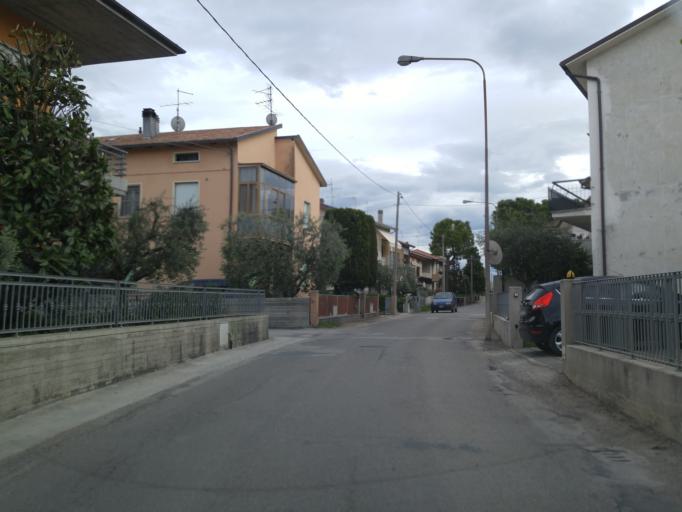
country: IT
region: The Marches
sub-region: Provincia di Pesaro e Urbino
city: Rosciano
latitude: 43.8265
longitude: 13.0060
